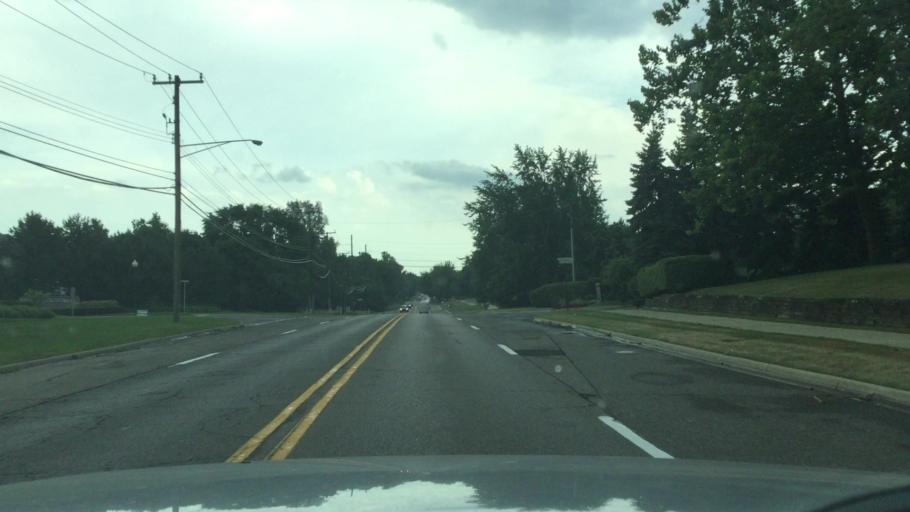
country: US
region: Michigan
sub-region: Oakland County
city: Keego Harbor
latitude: 42.6500
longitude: -83.3462
